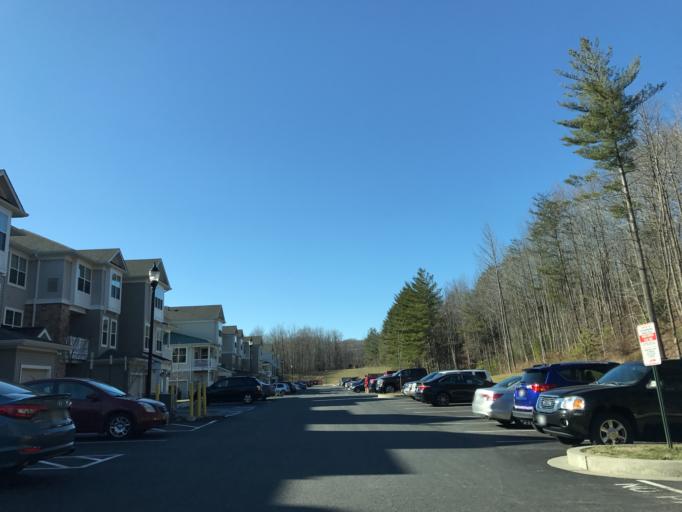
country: US
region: Maryland
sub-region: Harford County
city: Riverside
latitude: 39.4871
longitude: -76.2372
